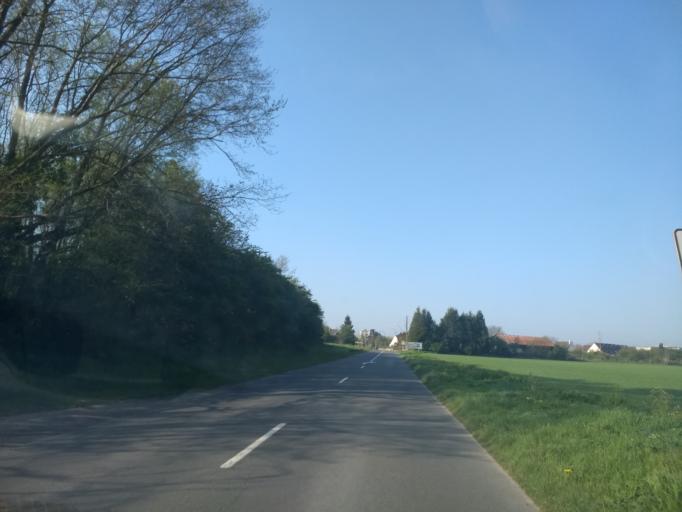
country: FR
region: Picardie
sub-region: Departement de la Somme
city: Rivery
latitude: 49.9169
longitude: 2.3220
